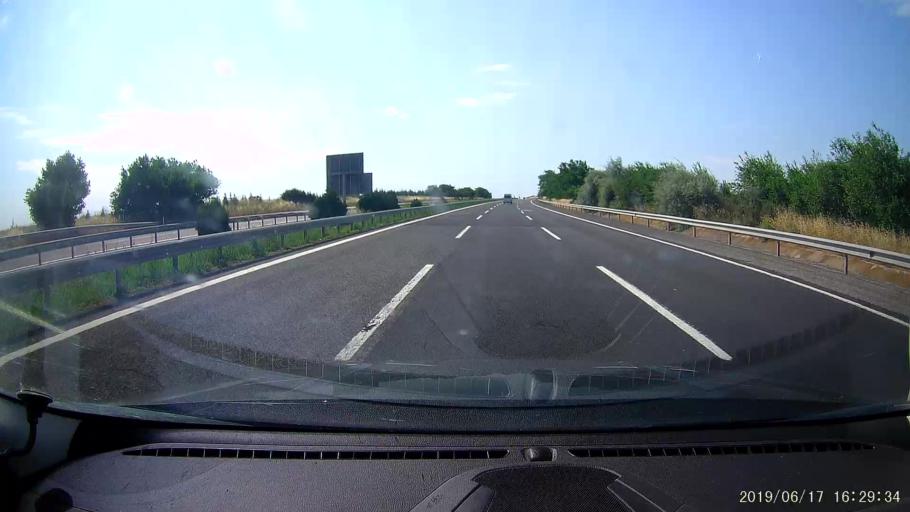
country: TR
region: Tekirdag
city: Beyazkoy
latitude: 41.3353
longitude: 27.6776
